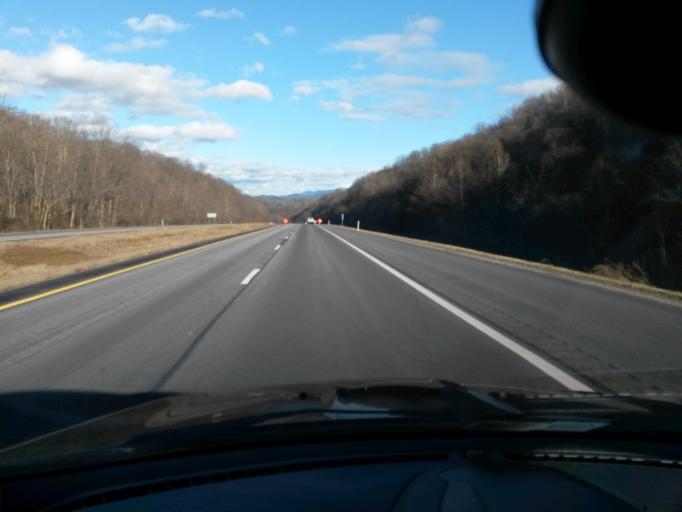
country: US
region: Virginia
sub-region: Giles County
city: Narrows
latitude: 37.3601
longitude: -80.8818
